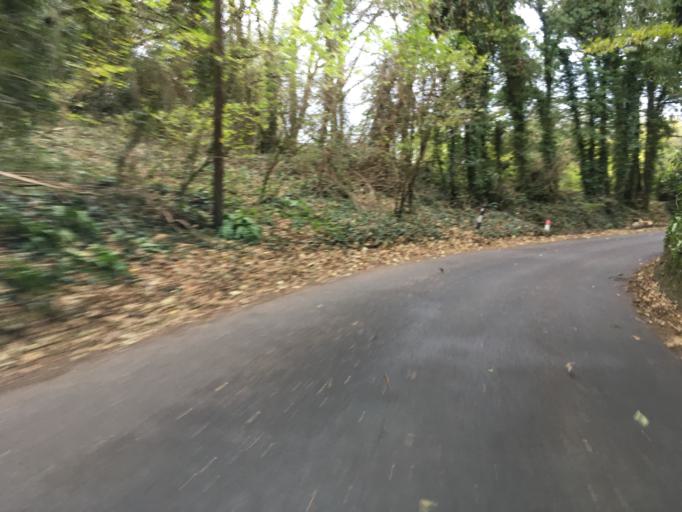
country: GB
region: England
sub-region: South Gloucestershire
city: Hinton
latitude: 51.4891
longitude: -2.3820
